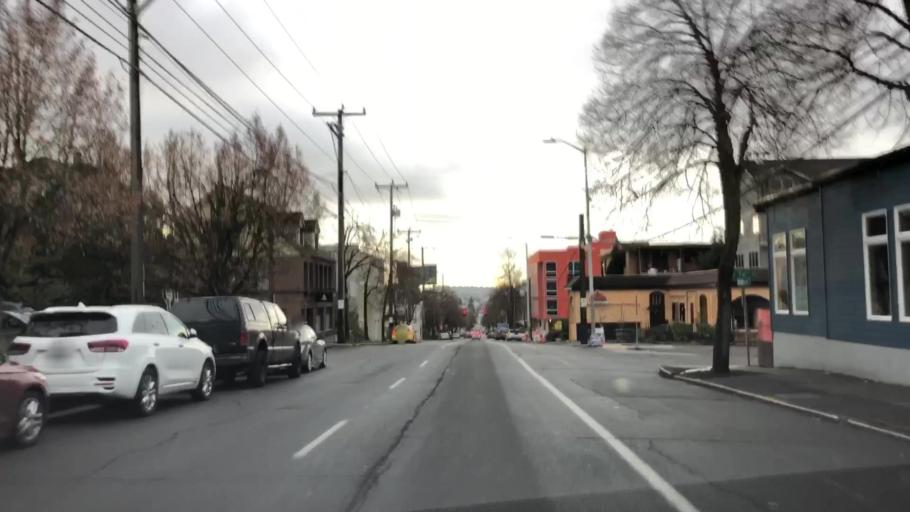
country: US
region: Washington
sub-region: King County
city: Seattle
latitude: 47.6812
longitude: -122.3175
